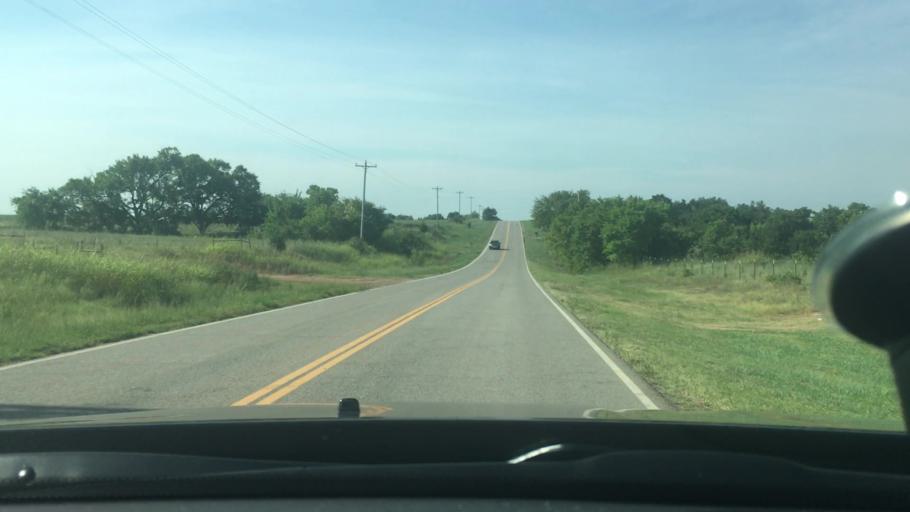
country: US
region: Oklahoma
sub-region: Garvin County
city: Maysville
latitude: 34.6741
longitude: -97.4054
